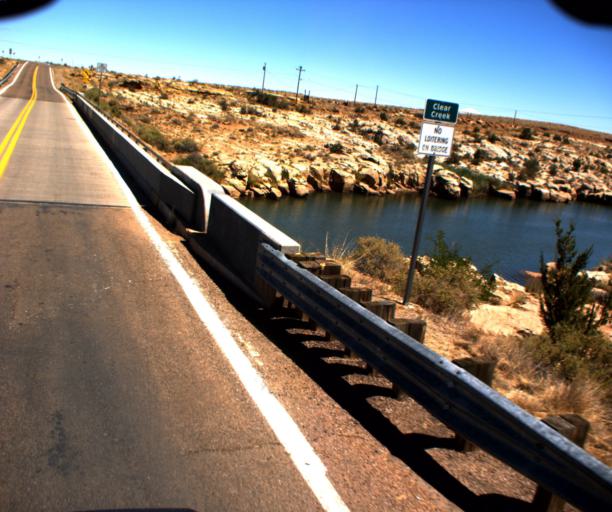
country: US
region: Arizona
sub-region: Navajo County
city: Winslow
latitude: 34.9677
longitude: -110.6466
